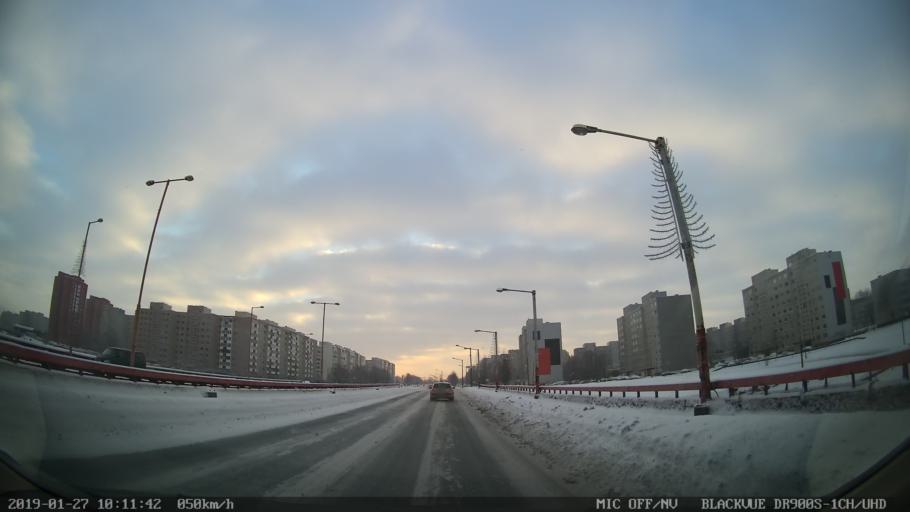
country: EE
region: Harju
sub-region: Tallinna linn
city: Kose
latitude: 59.4396
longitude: 24.8253
